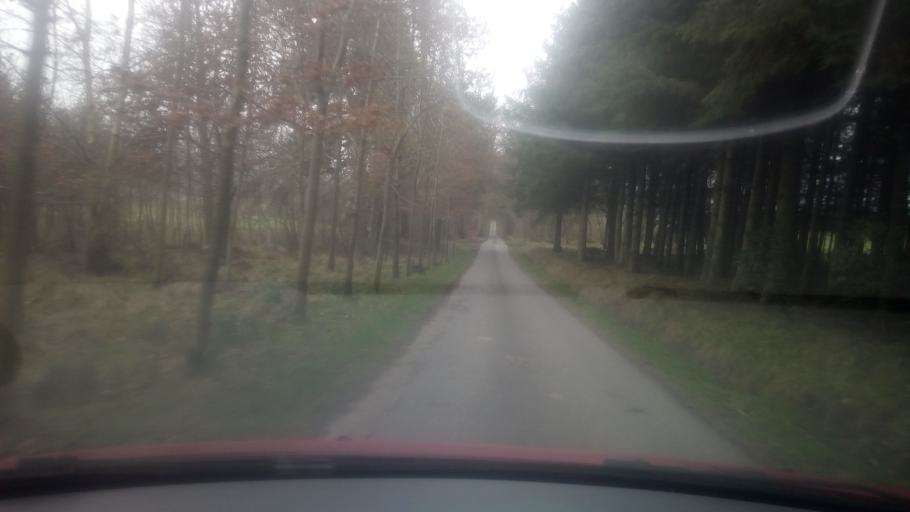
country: GB
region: Scotland
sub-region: The Scottish Borders
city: Jedburgh
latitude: 55.4344
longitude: -2.6402
